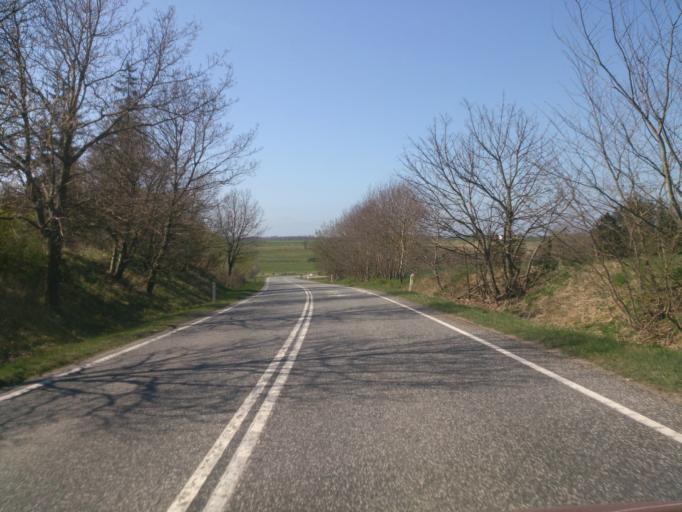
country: DK
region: Central Jutland
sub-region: Viborg Kommune
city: Bjerringbro
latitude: 56.4172
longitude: 9.6733
